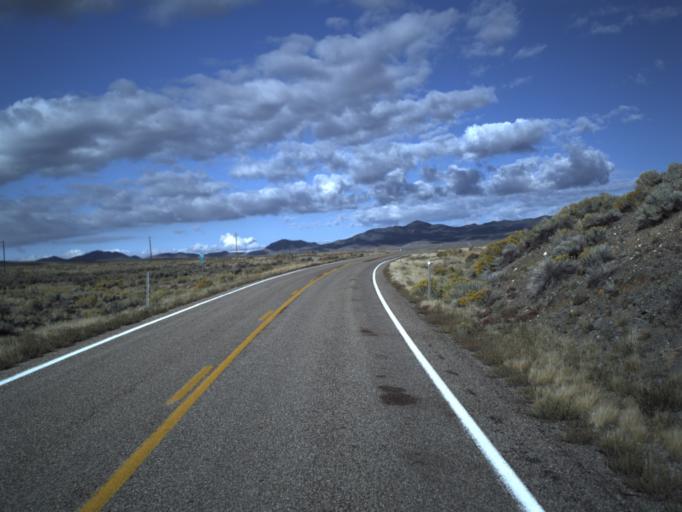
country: US
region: Utah
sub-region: Beaver County
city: Milford
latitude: 38.4241
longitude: -113.1129
